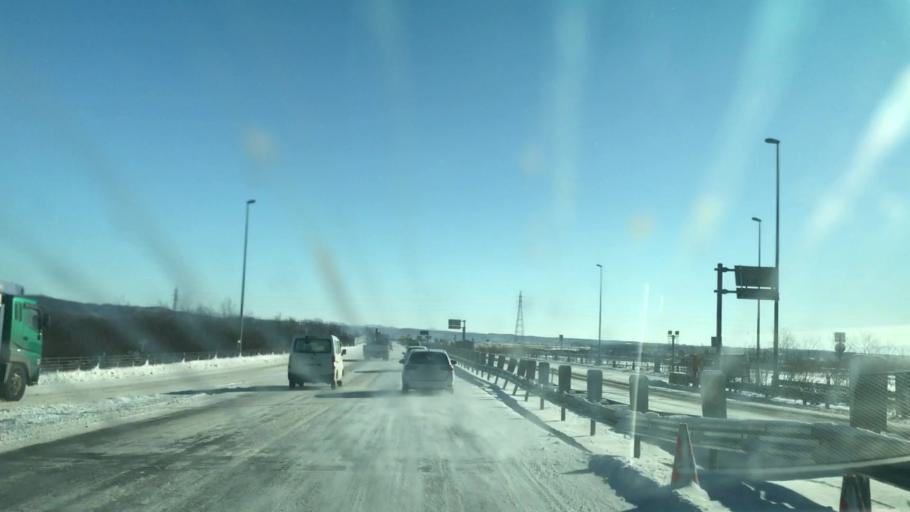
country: JP
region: Hokkaido
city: Tomakomai
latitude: 42.5879
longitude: 141.9310
